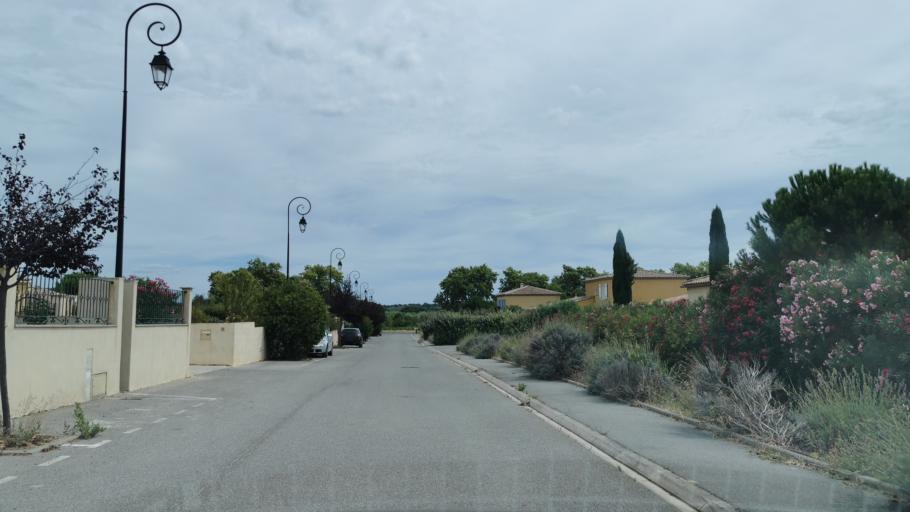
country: FR
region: Languedoc-Roussillon
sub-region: Departement de l'Aude
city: Bize-Minervois
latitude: 43.2996
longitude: 2.8260
